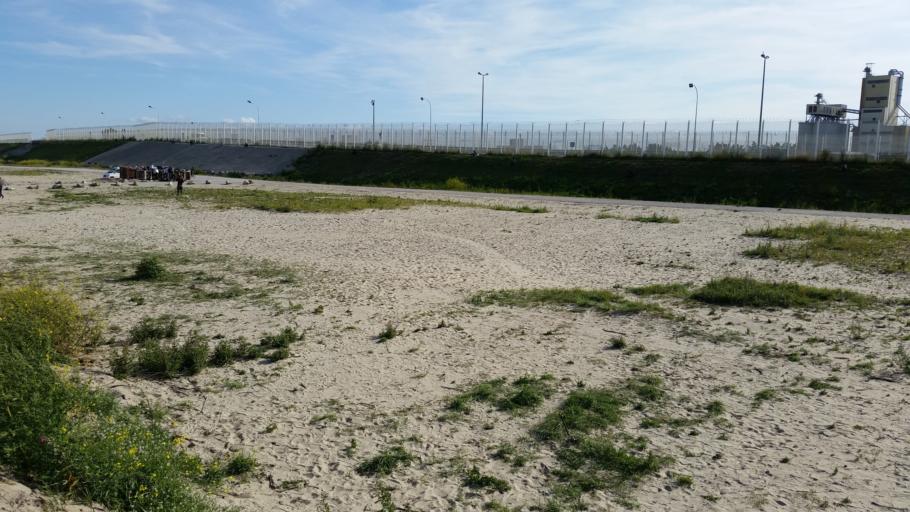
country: FR
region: Nord-Pas-de-Calais
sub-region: Departement du Pas-de-Calais
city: Marck
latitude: 50.9720
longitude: 1.9019
